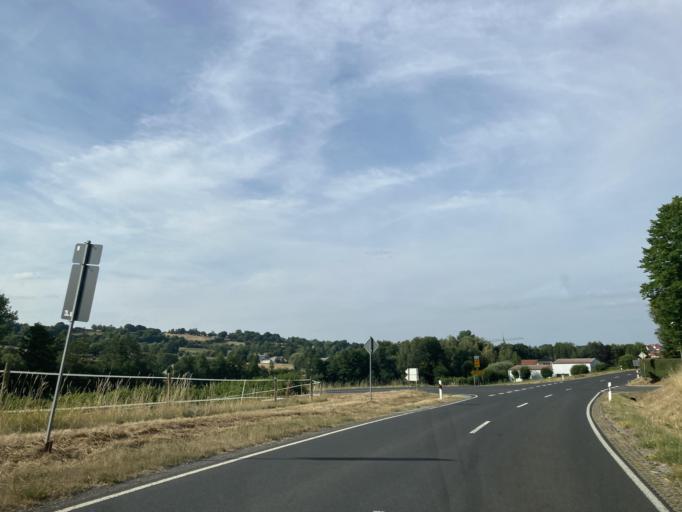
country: DE
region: Hesse
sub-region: Regierungsbezirk Kassel
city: Hosenfeld
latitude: 50.4976
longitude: 9.4732
